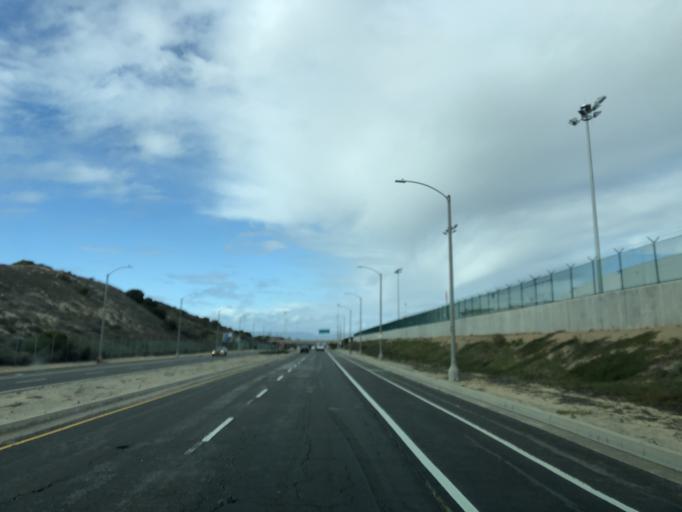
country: US
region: California
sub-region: Los Angeles County
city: El Segundo
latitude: 33.9363
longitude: -118.4317
